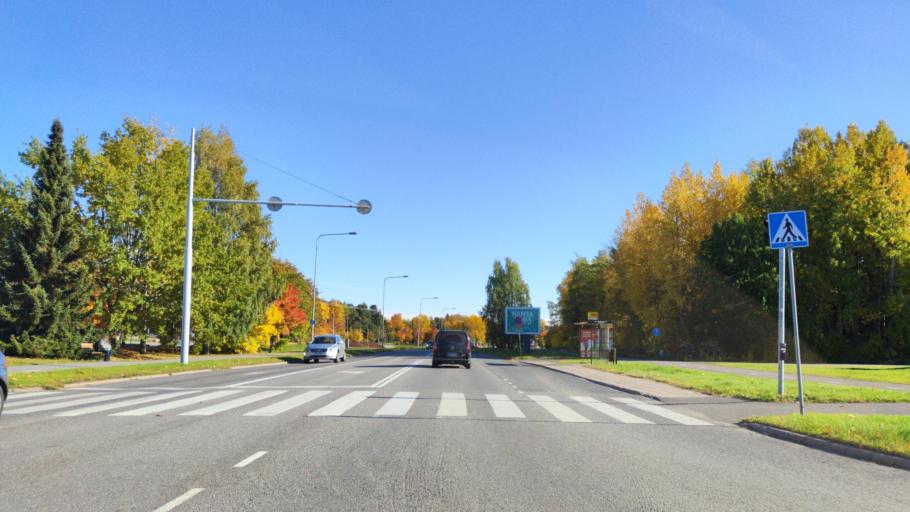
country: FI
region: Varsinais-Suomi
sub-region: Turku
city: Turku
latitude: 60.4772
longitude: 22.2505
